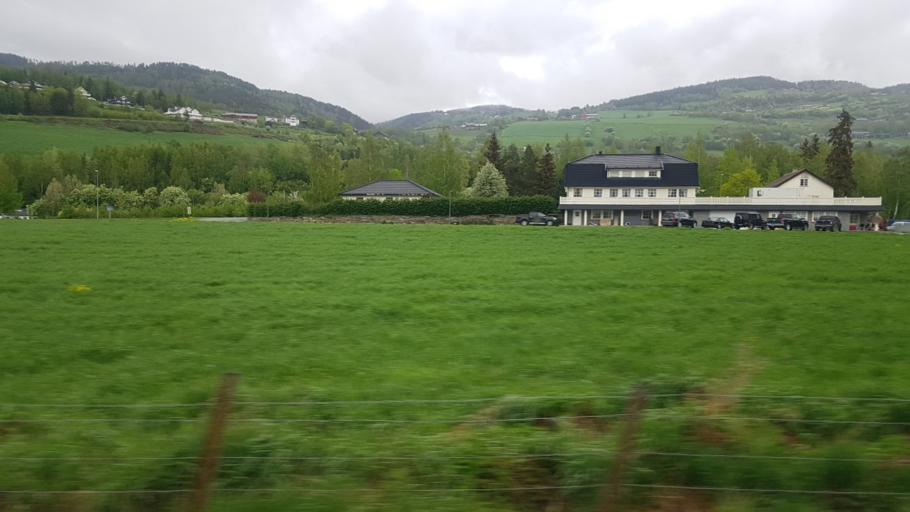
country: NO
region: Oppland
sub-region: Nord-Fron
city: Vinstra
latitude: 61.5801
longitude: 9.7641
